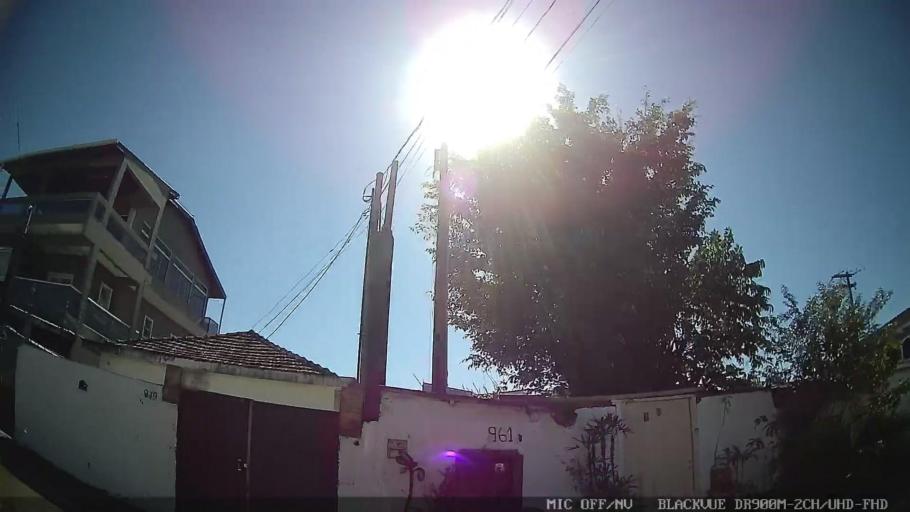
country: BR
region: Sao Paulo
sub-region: Guaruja
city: Guaruja
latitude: -23.9605
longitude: -46.2751
